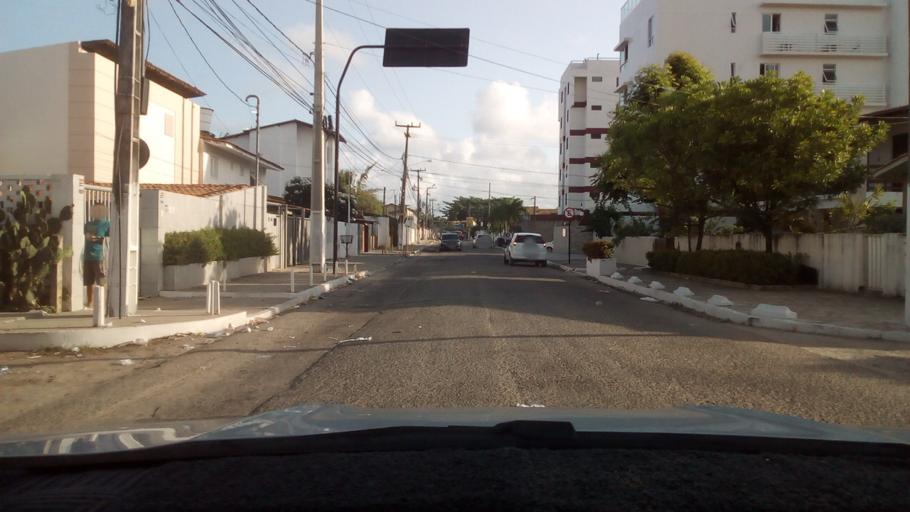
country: BR
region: Paraiba
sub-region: Cabedelo
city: Cabedelo
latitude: -7.0225
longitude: -34.8304
